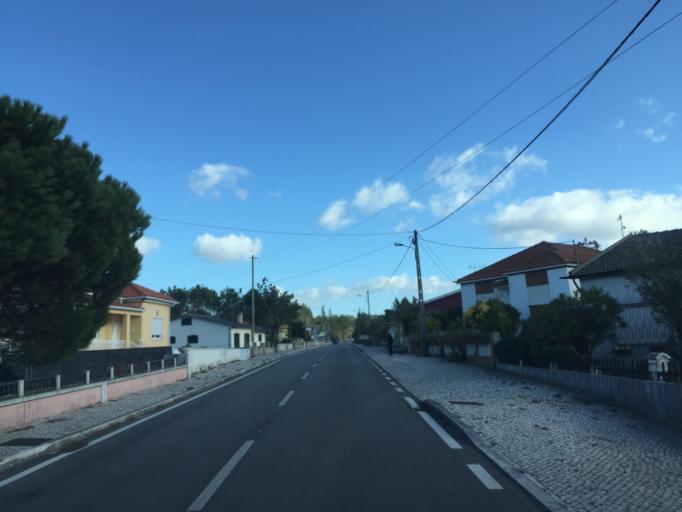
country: PT
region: Coimbra
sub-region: Figueira da Foz
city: Tavarede
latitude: 40.2102
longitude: -8.8451
